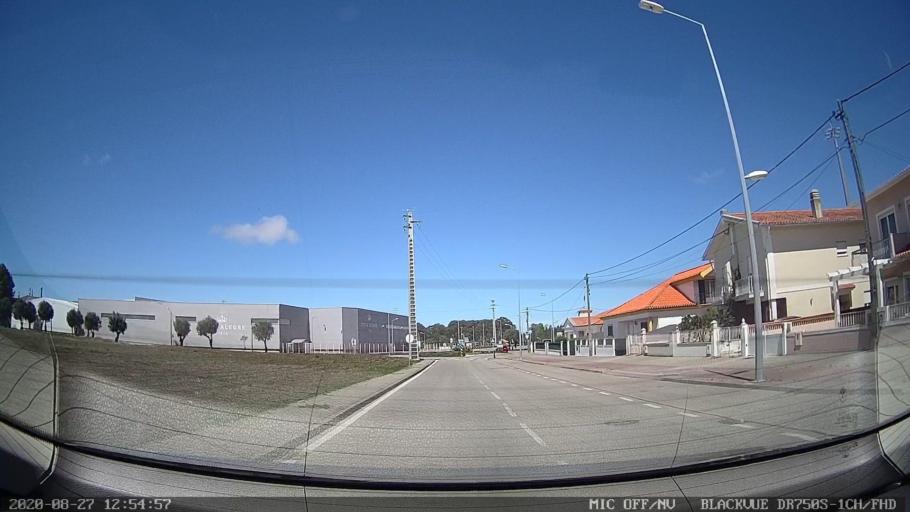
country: PT
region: Aveiro
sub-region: Ilhavo
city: Ilhavo
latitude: 40.5900
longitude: -8.6807
